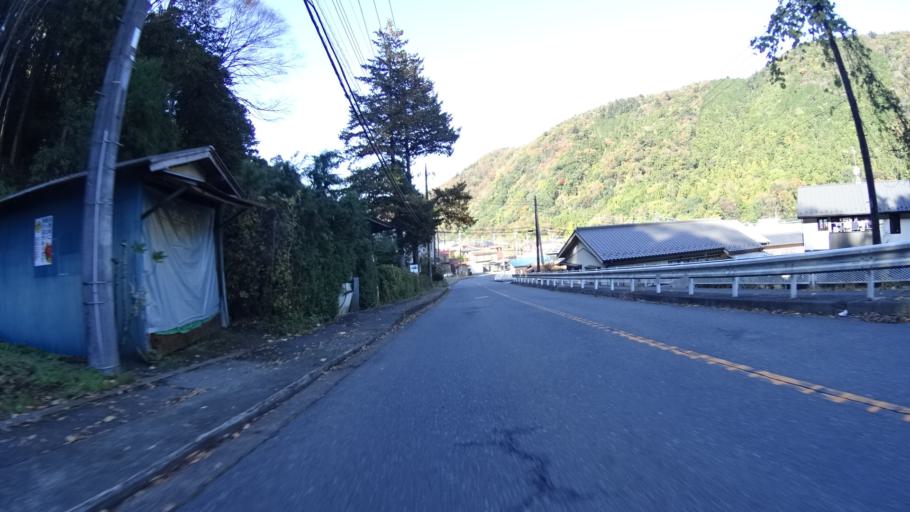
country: JP
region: Tokyo
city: Hachioji
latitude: 35.5409
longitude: 139.2715
